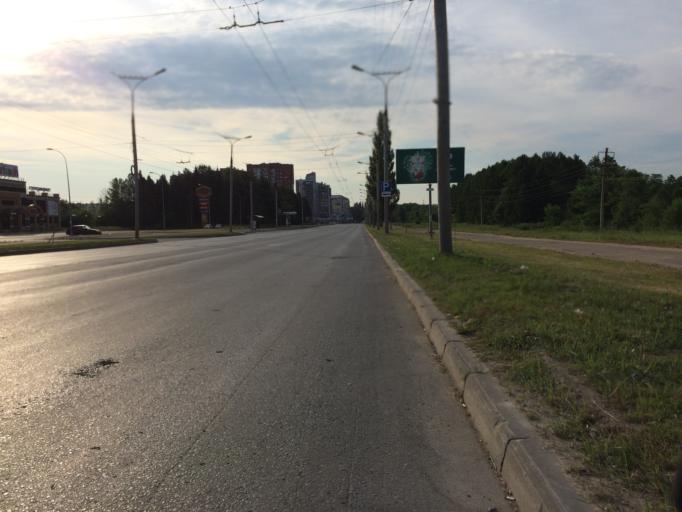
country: RU
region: Mariy-El
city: Yoshkar-Ola
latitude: 56.6248
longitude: 47.9272
